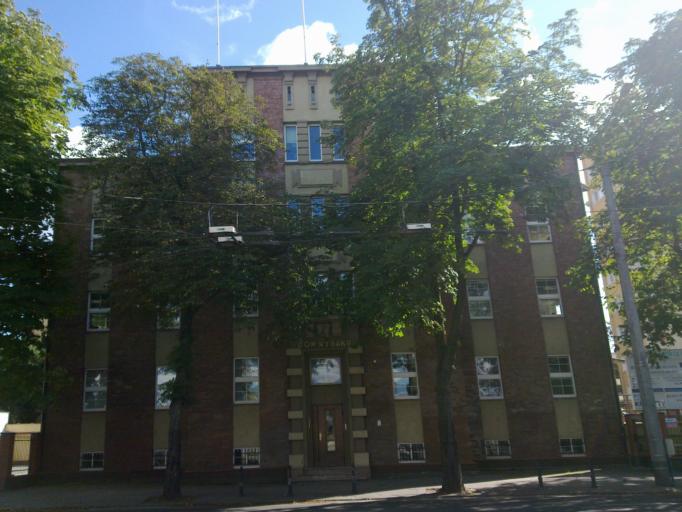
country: PL
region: Pomeranian Voivodeship
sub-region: Gdynia
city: Gdynia
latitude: 54.5234
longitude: 18.5374
